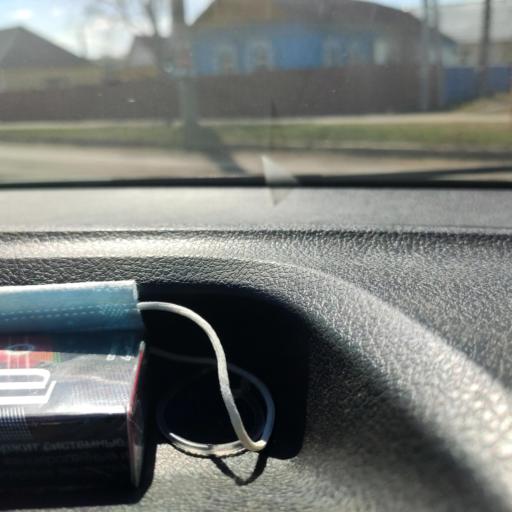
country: RU
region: Bashkortostan
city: Alekseyevka
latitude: 54.6918
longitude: 55.0099
